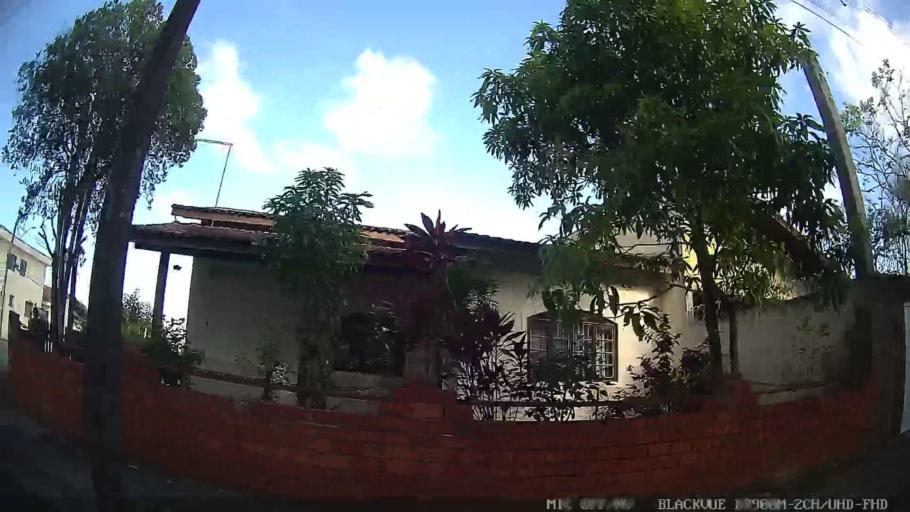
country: BR
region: Sao Paulo
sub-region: Peruibe
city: Peruibe
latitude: -24.2875
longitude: -46.9682
